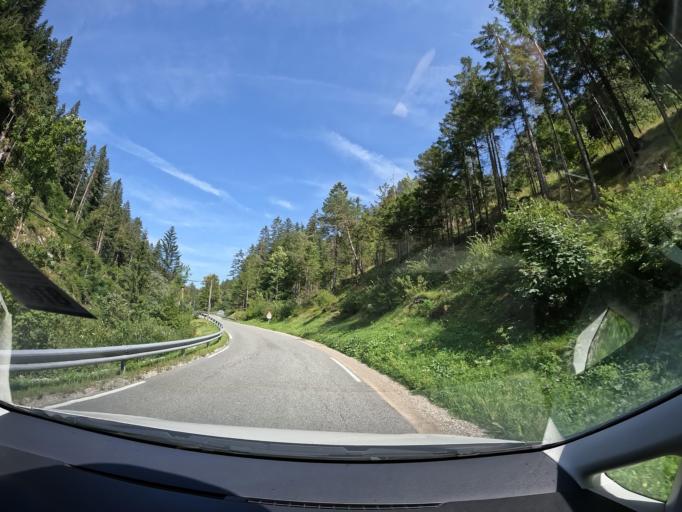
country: SI
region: Jesenice
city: Koroska Bela
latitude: 46.4797
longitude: 14.1015
